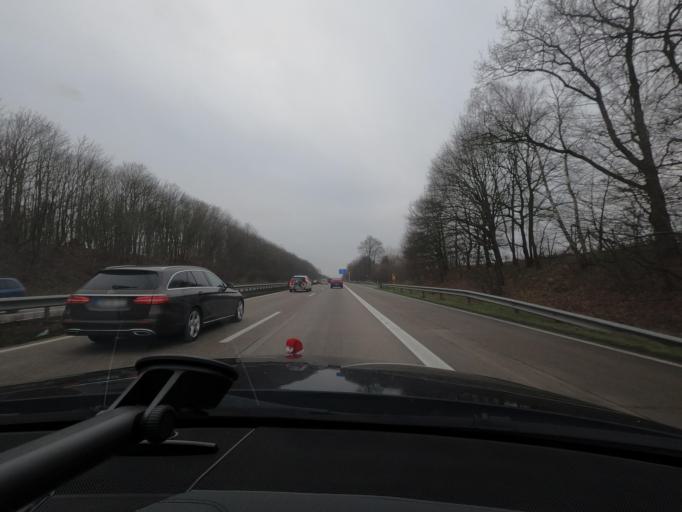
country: DE
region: Lower Saxony
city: Bad Fallingbostel
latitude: 52.8605
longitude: 9.7177
